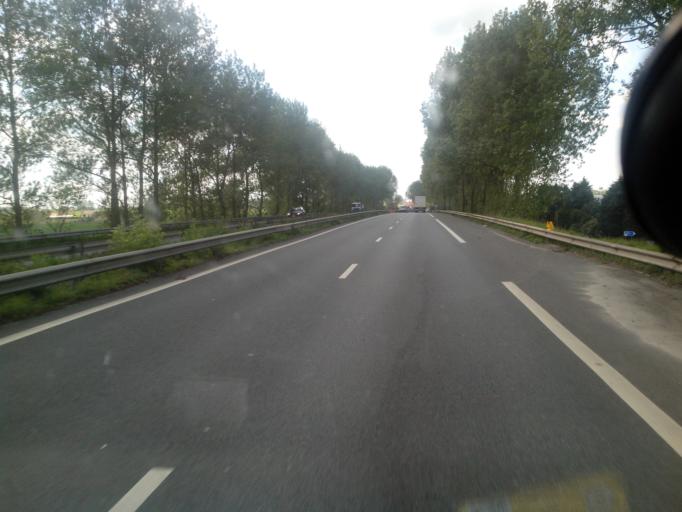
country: FR
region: Nord-Pas-de-Calais
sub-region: Departement du Nord
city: Socx
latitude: 50.9512
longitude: 2.4226
